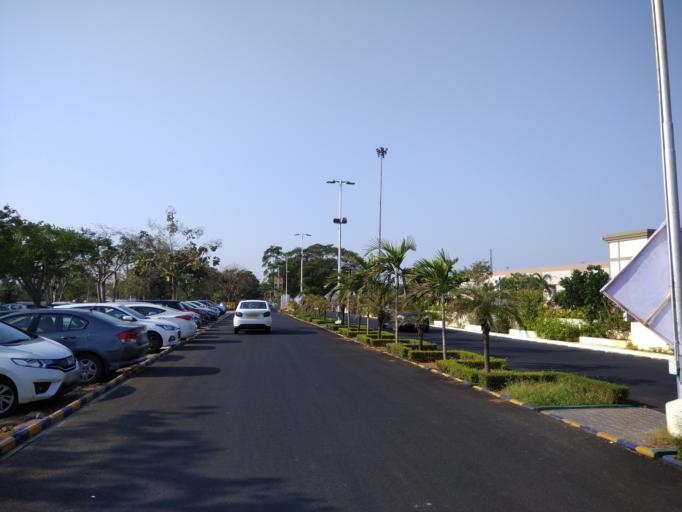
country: IN
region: Tamil Nadu
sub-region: Kancheepuram
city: Saint Thomas Mount
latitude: 13.0132
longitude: 80.1895
